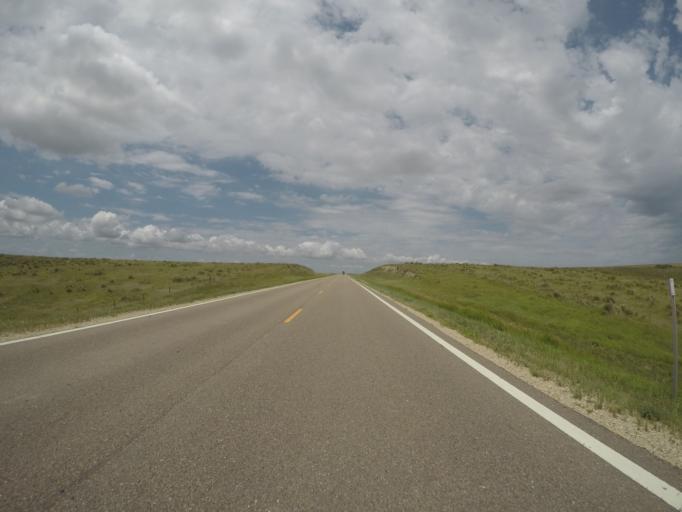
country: US
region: Kansas
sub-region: Rawlins County
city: Atwood
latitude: 39.7599
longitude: -101.0471
